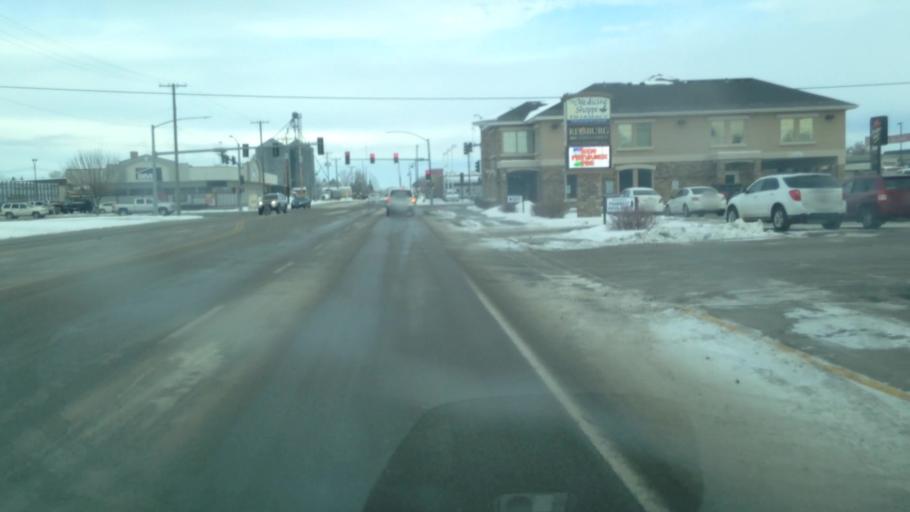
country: US
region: Idaho
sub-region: Madison County
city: Rexburg
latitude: 43.8251
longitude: -111.7895
